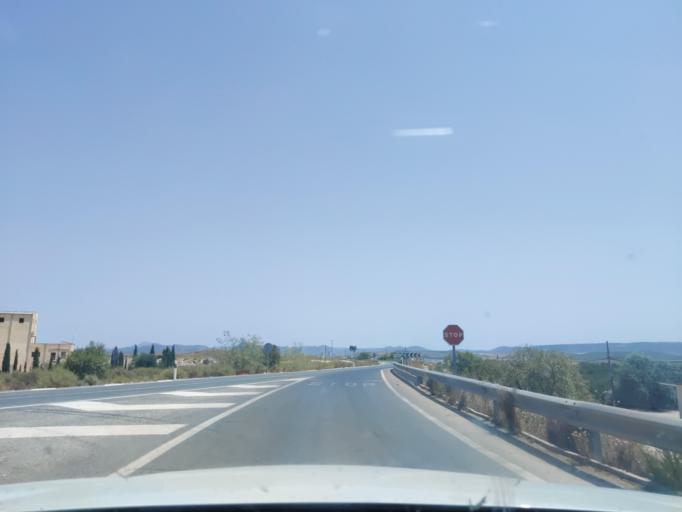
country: ES
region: Castille-La Mancha
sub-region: Provincia de Albacete
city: Hellin
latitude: 38.5009
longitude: -1.6732
